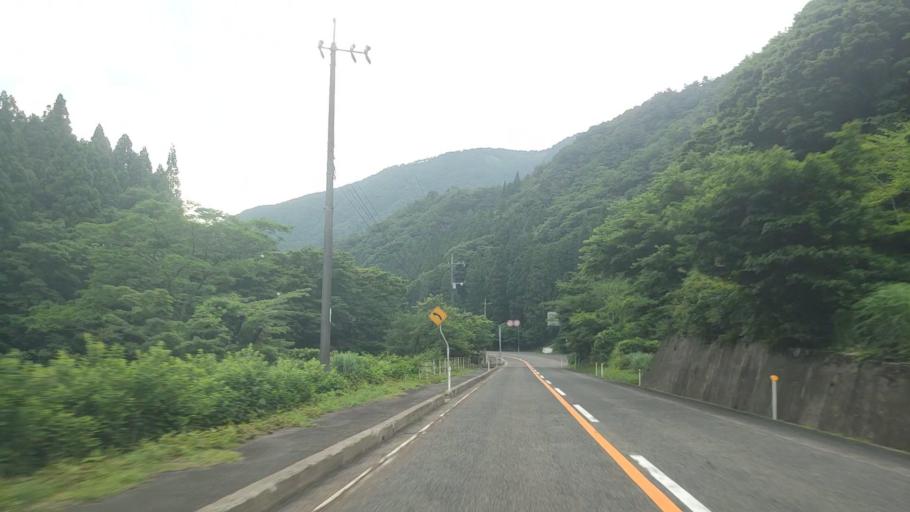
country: JP
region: Tottori
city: Kurayoshi
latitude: 35.3168
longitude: 133.8987
